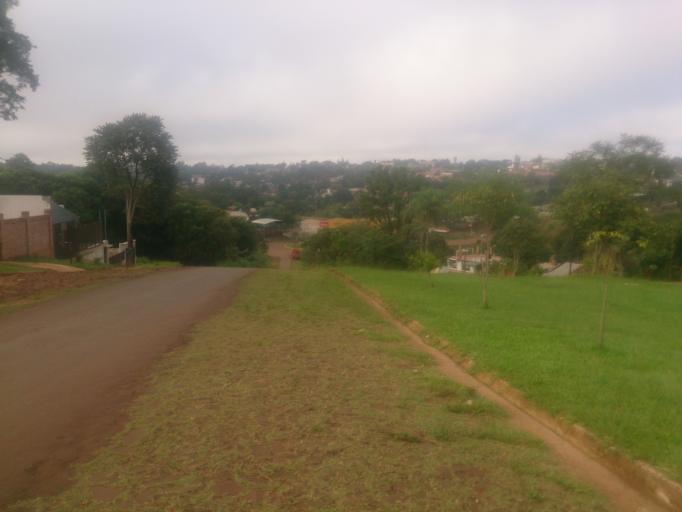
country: AR
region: Misiones
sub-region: Departamento de Obera
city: Obera
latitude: -27.4773
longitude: -55.1064
